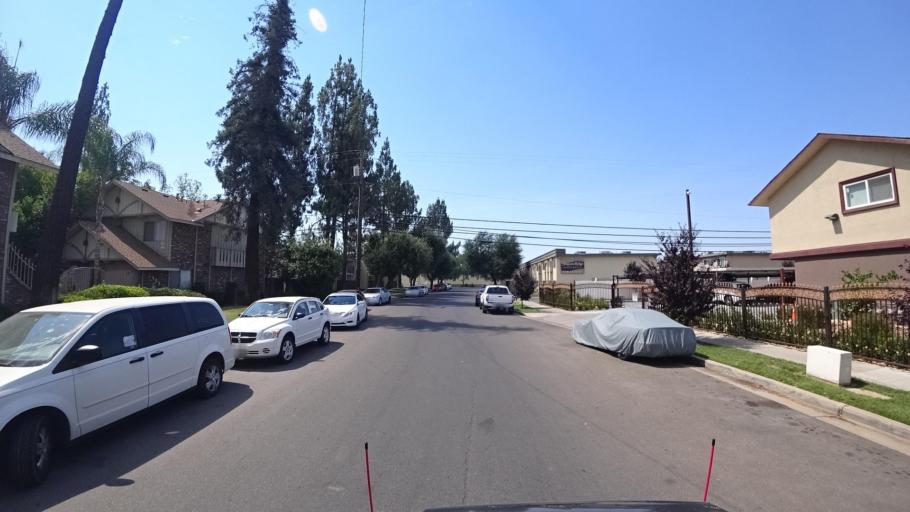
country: US
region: California
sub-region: Fresno County
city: Sunnyside
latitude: 36.7396
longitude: -119.6971
